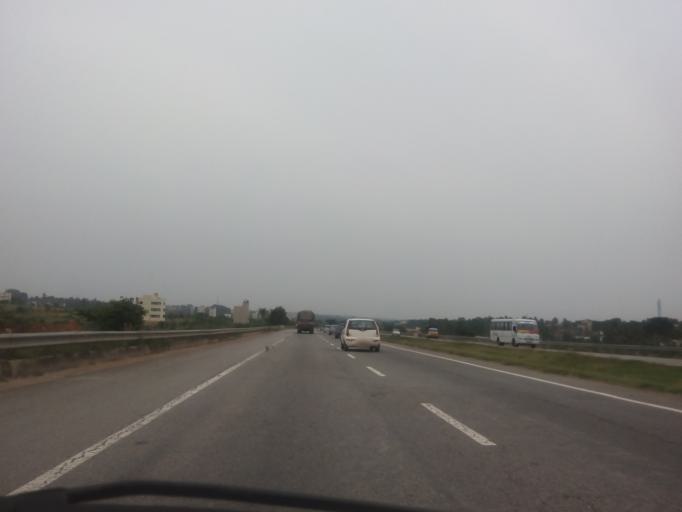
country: IN
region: Karnataka
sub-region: Bangalore Urban
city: Bangalore
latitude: 12.9591
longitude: 77.4715
